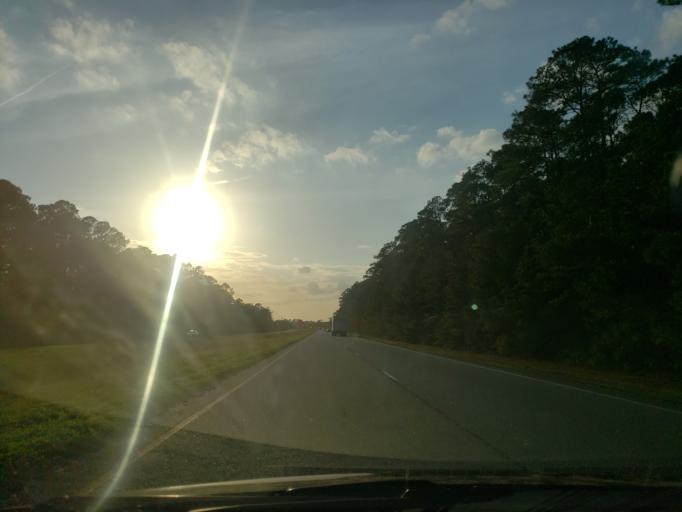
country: US
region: Georgia
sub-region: Chatham County
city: Bloomingdale
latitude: 32.1482
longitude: -81.2920
